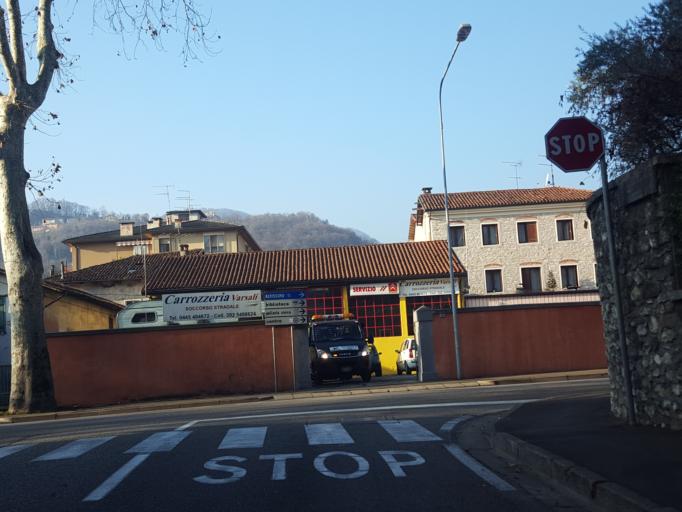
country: IT
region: Veneto
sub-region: Provincia di Vicenza
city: Valdagno
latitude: 45.6405
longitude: 11.3013
